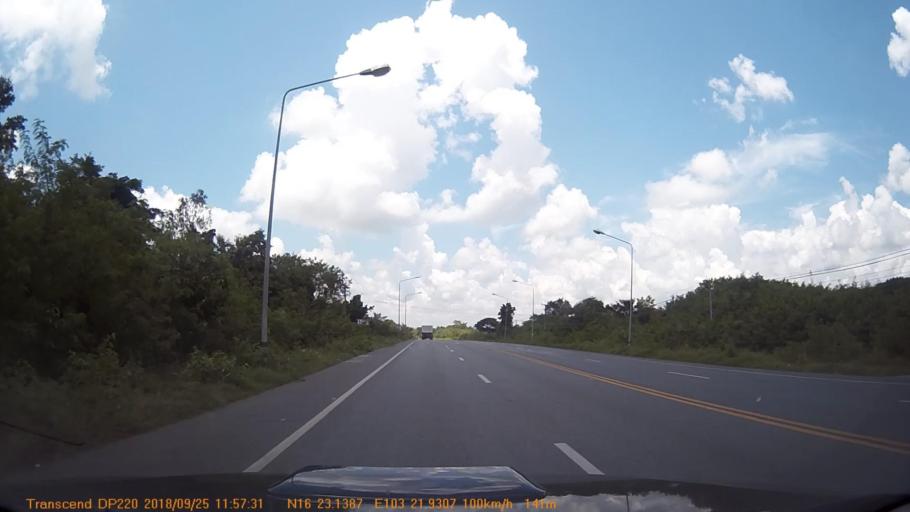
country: TH
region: Kalasin
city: Yang Talat
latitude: 16.3856
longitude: 103.3656
